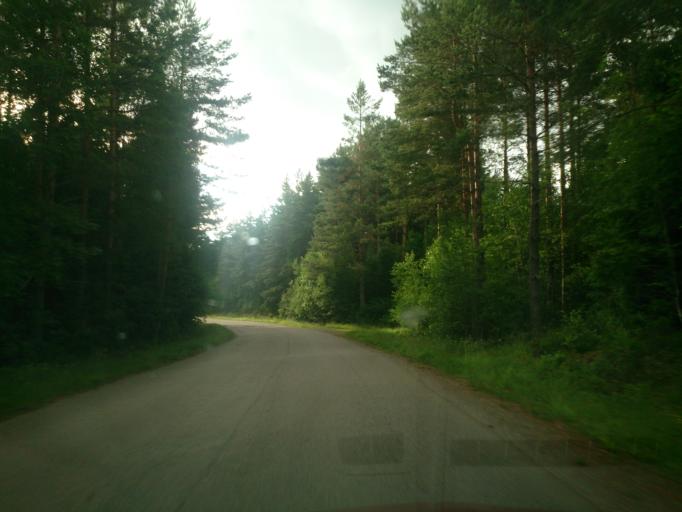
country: SE
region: OEstergoetland
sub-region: Norrkopings Kommun
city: Jursla
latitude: 58.7223
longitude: 16.1333
